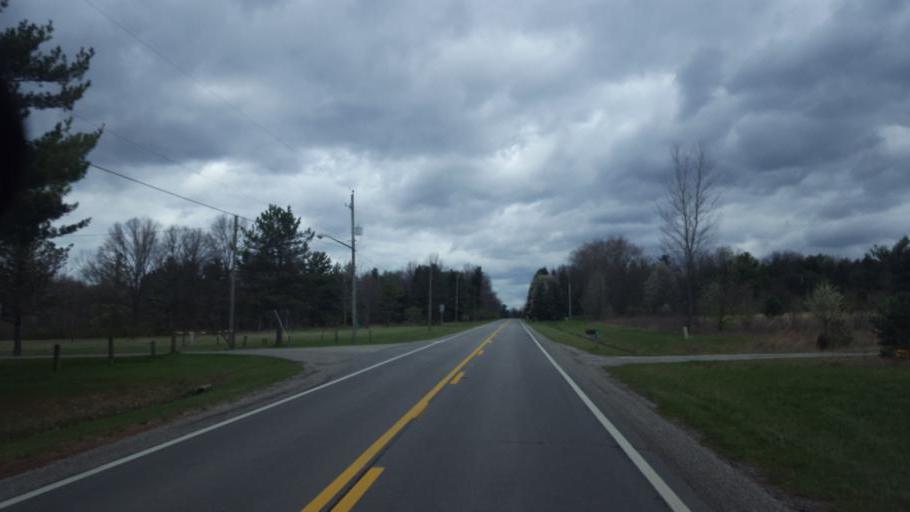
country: US
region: Ohio
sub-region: Franklin County
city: Huber Ridge
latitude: 40.1101
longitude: -82.8723
